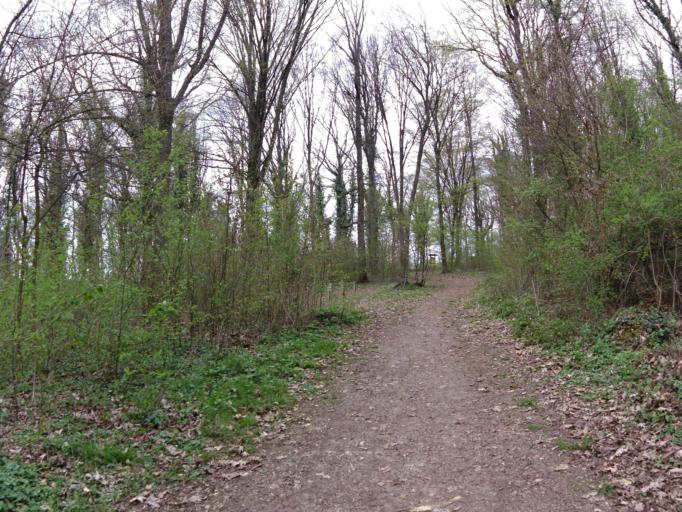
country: DE
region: Bavaria
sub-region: Regierungsbezirk Unterfranken
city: Rottendorf
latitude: 49.7986
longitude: 10.0119
